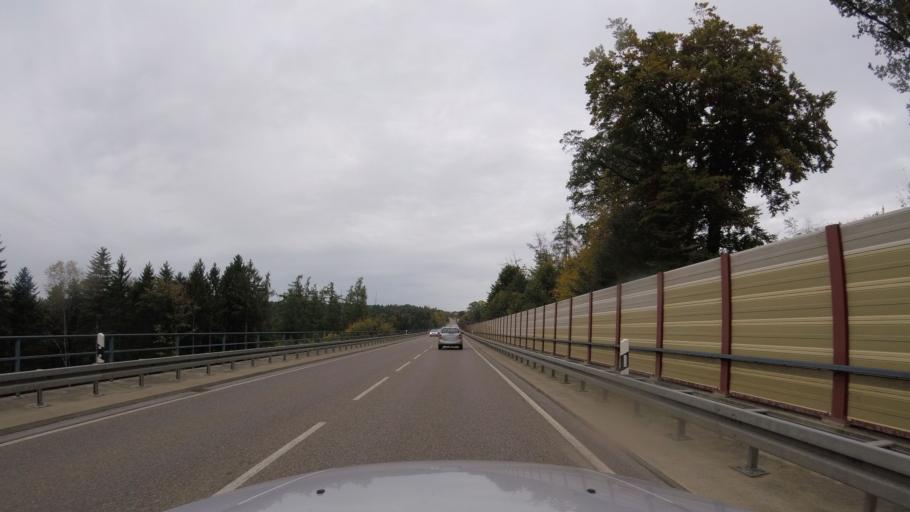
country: DE
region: Baden-Wuerttemberg
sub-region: Regierungsbezirk Stuttgart
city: Mutlangen
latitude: 48.8241
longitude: 9.7838
